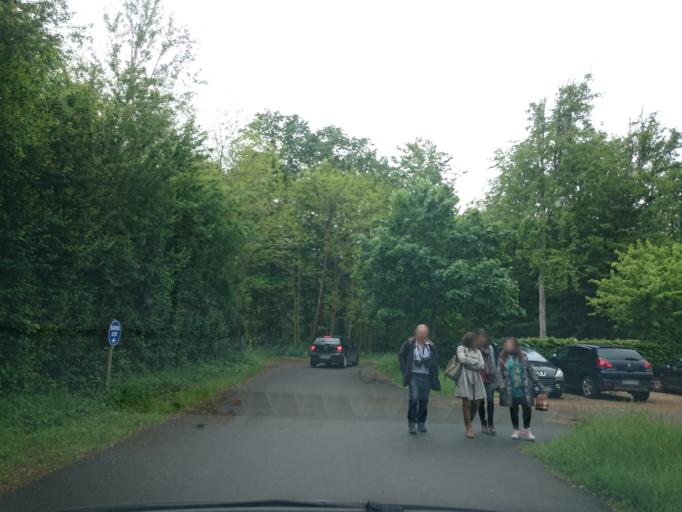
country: FR
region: Centre
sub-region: Departement du Loir-et-Cher
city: Saint-Dye-sur-Loire
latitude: 47.6146
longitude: 1.5107
